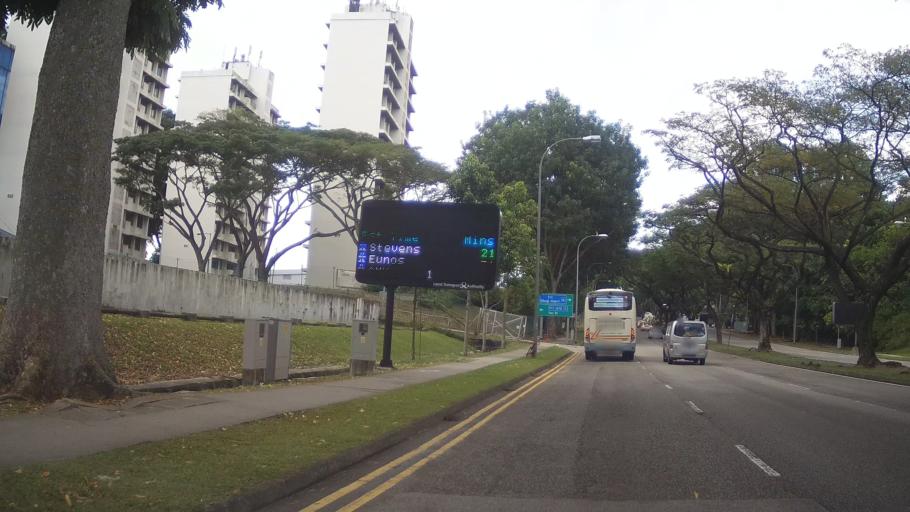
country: MY
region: Johor
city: Johor Bahru
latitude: 1.3302
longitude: 103.6779
